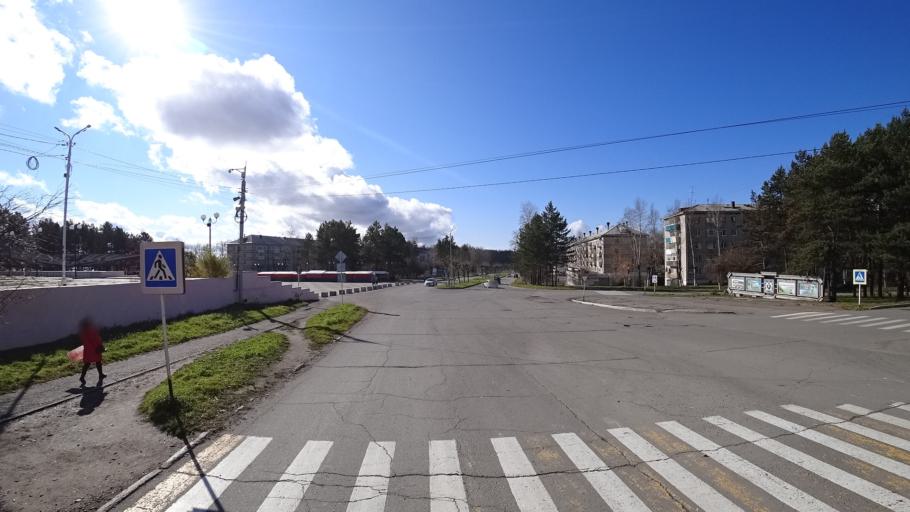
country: RU
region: Khabarovsk Krai
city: Amursk
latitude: 50.2272
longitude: 136.9103
